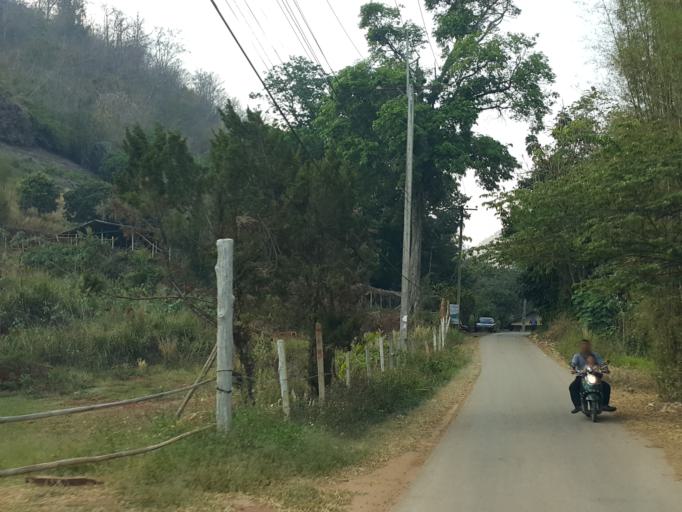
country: TH
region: Chiang Mai
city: Samoeng
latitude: 18.8940
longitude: 98.8325
